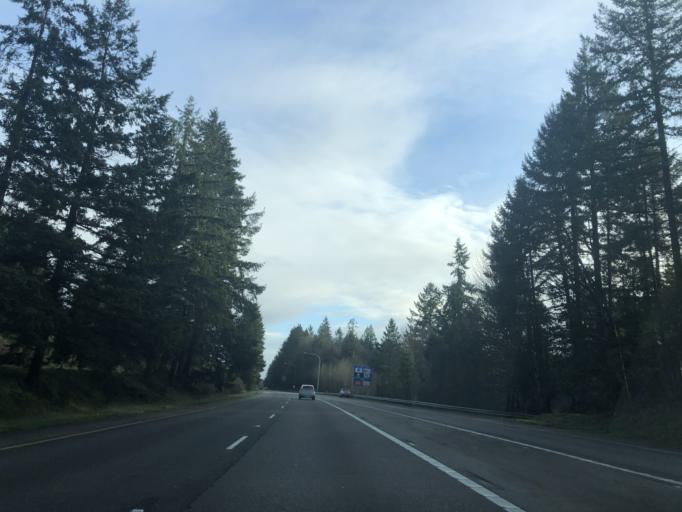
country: US
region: Washington
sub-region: Kitsap County
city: Port Orchard
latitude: 47.5173
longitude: -122.6582
